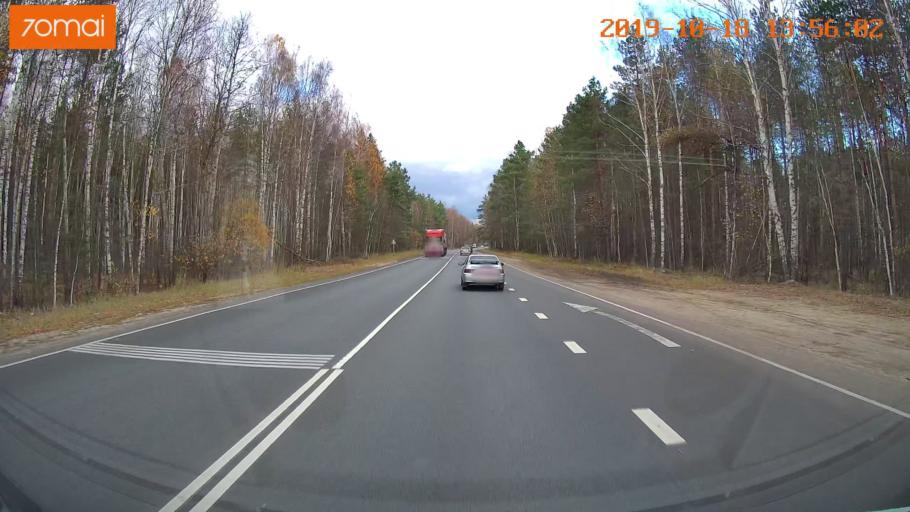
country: RU
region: Rjazan
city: Spas-Klepiki
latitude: 55.0592
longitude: 40.0268
